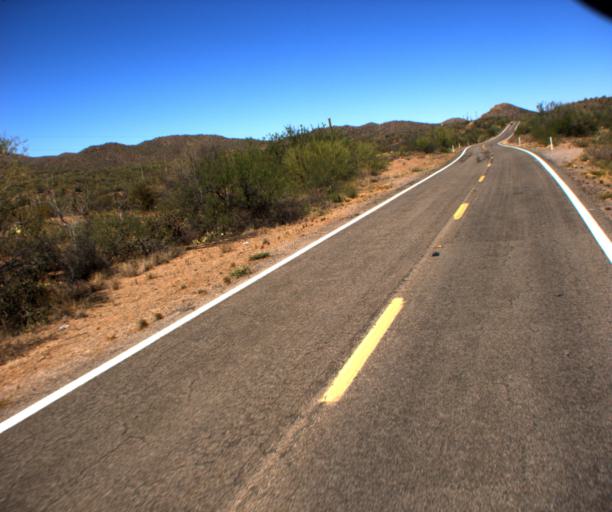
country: US
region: Arizona
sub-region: Pima County
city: Sells
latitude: 32.1691
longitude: -112.1370
